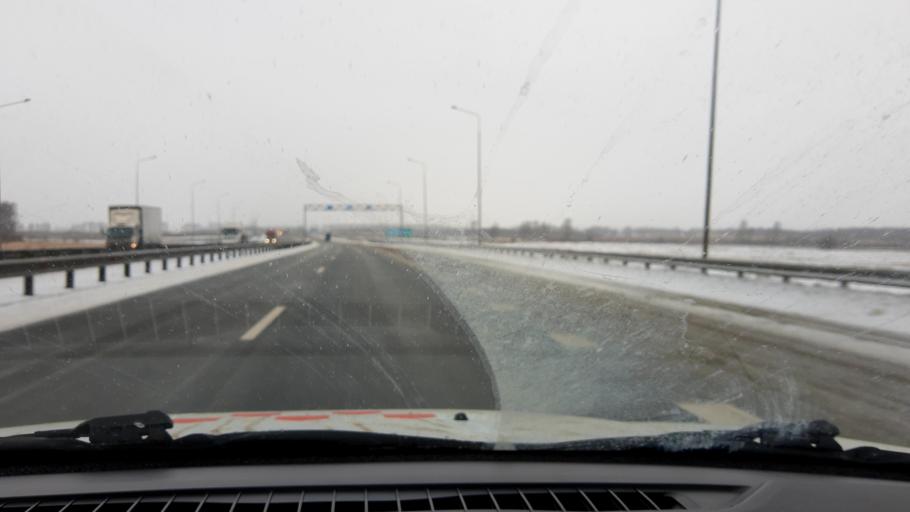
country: RU
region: Nizjnij Novgorod
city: Burevestnik
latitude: 56.1186
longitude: 43.9264
